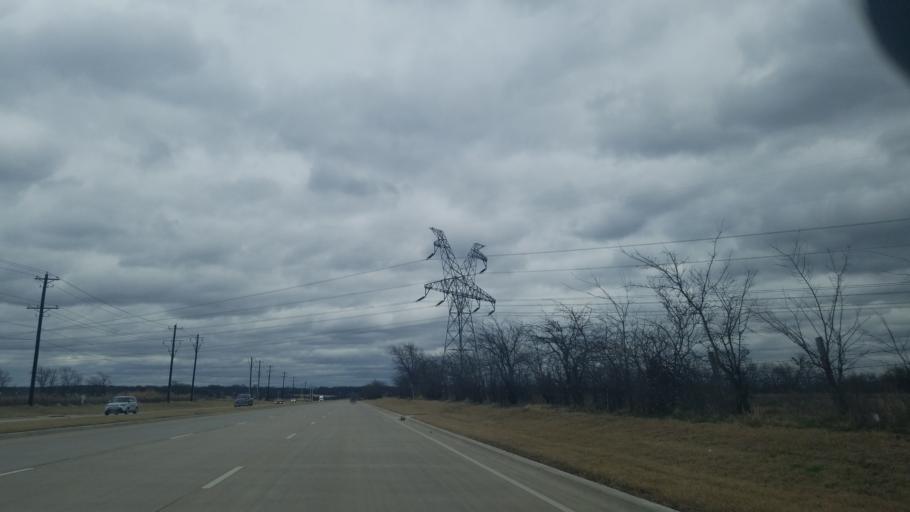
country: US
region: Texas
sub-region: Denton County
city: Trophy Club
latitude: 33.0525
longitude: -97.1947
